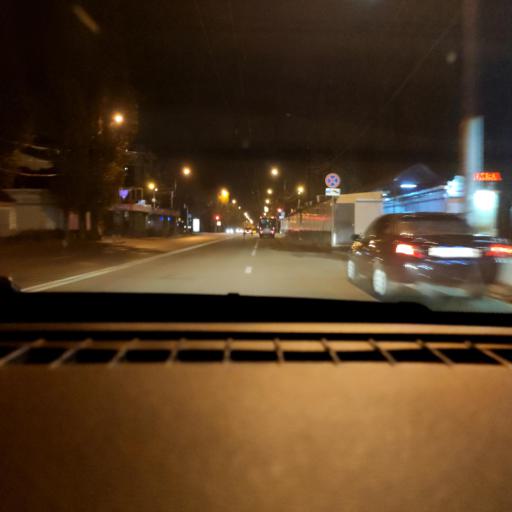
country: RU
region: Voronezj
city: Podgornoye
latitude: 51.7077
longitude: 39.1740
